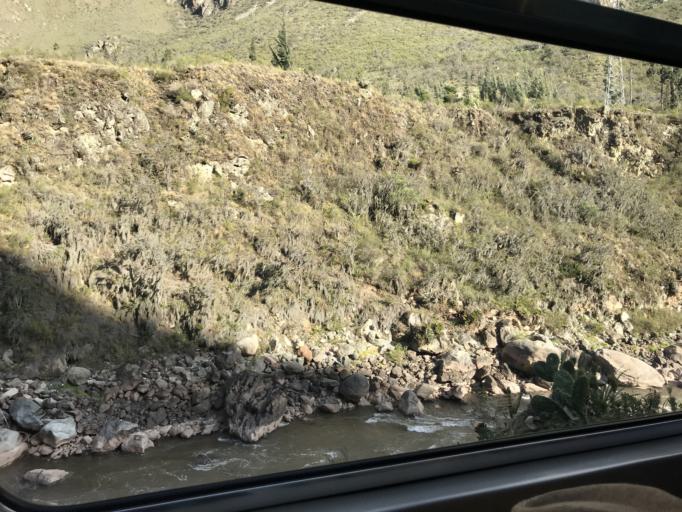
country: PE
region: Cusco
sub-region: Provincia de Urubamba
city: Ollantaytambo
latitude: -13.2231
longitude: -72.3956
